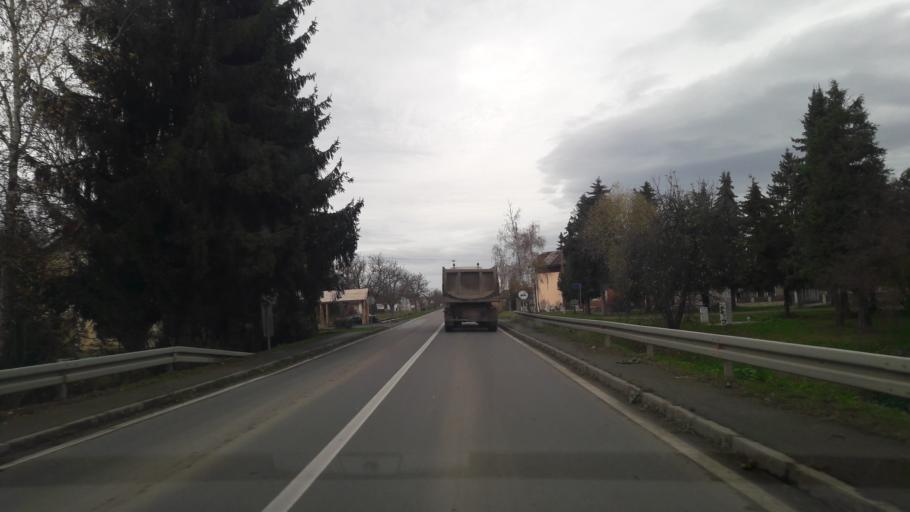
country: HR
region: Osjecko-Baranjska
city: Fericanci
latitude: 45.5249
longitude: 17.9657
